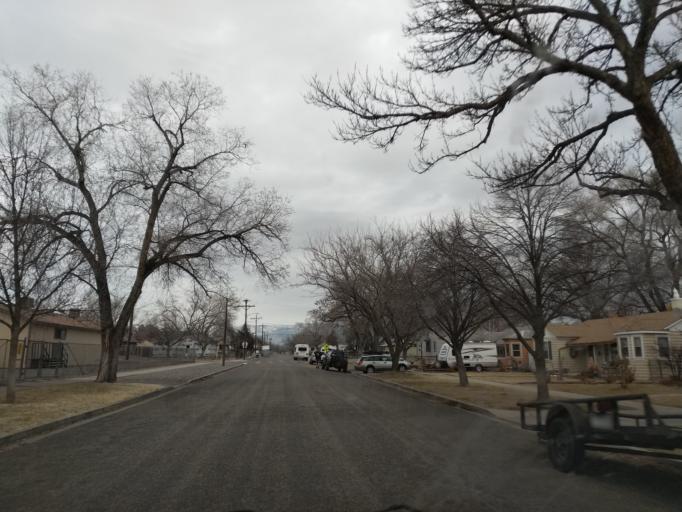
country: US
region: Colorado
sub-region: Mesa County
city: Grand Junction
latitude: 39.0723
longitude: -108.5486
